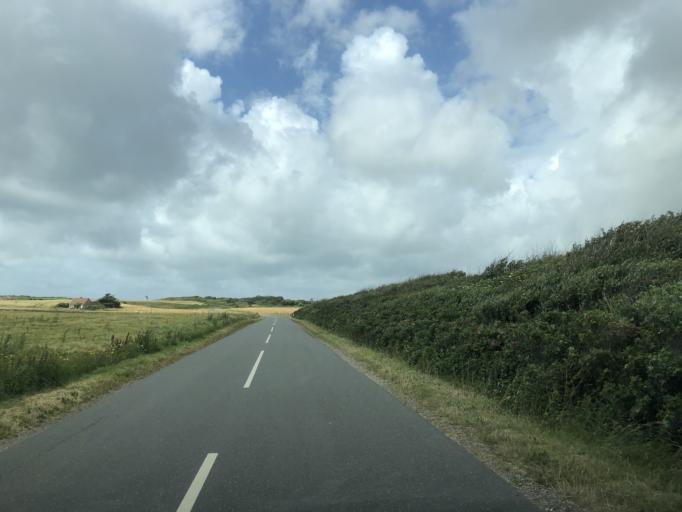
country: DK
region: Central Jutland
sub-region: Lemvig Kommune
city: Harboore
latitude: 56.4895
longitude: 8.1375
